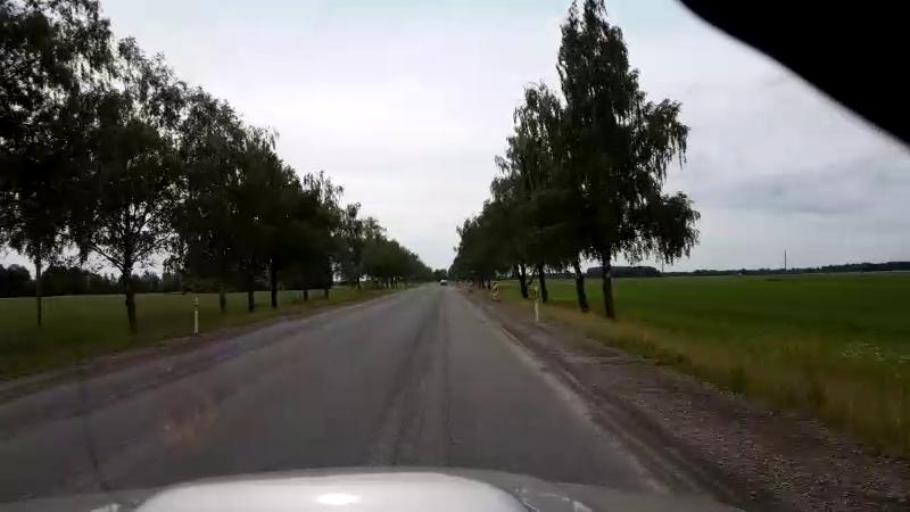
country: LV
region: Bauskas Rajons
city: Bauska
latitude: 56.3472
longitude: 24.2893
